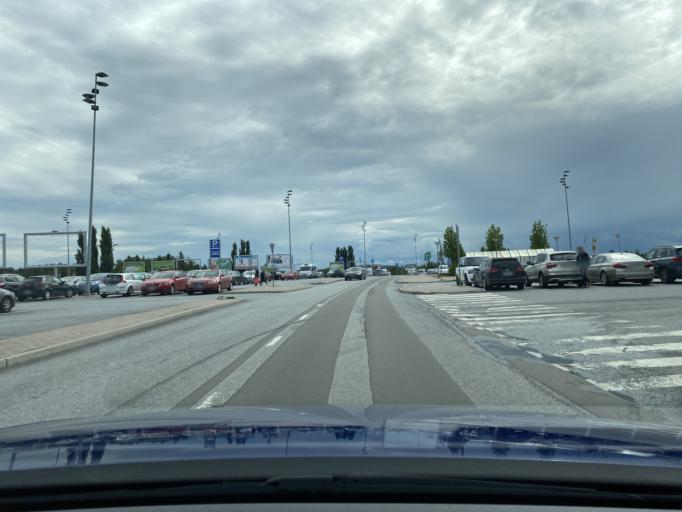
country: FI
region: Pirkanmaa
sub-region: Tampere
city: Lempaeaelae
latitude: 61.3594
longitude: 23.7973
